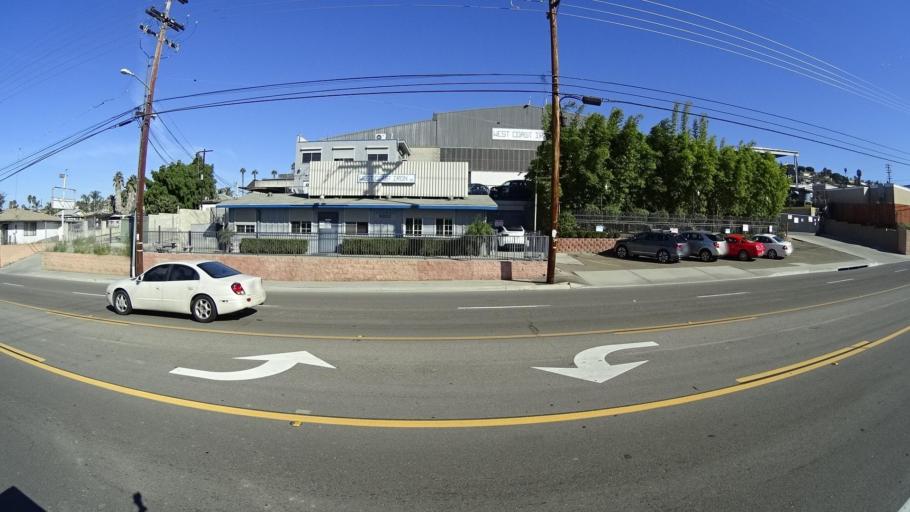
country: US
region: California
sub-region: San Diego County
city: La Presa
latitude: 32.7148
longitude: -116.9993
